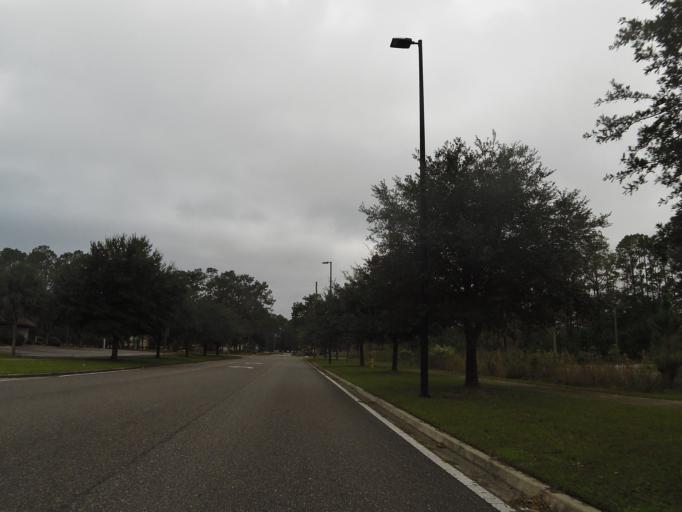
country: US
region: Florida
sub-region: Duval County
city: Baldwin
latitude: 30.2337
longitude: -81.8884
